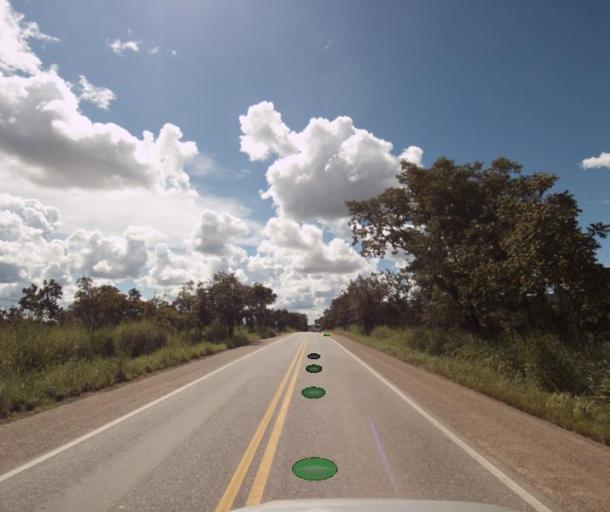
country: BR
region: Goias
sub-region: Porangatu
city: Porangatu
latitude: -13.6628
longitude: -49.0325
